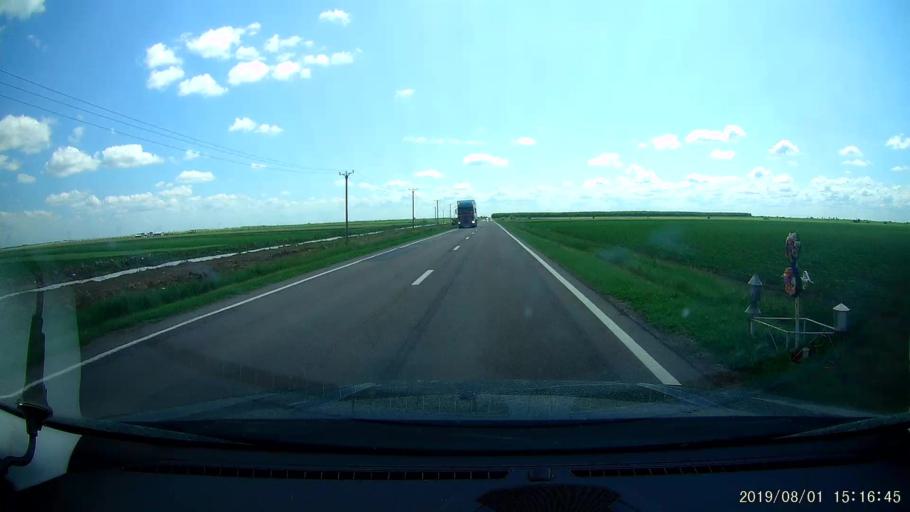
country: RO
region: Braila
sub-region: Comuna Unirea
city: Unirea
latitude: 45.1412
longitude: 27.8476
